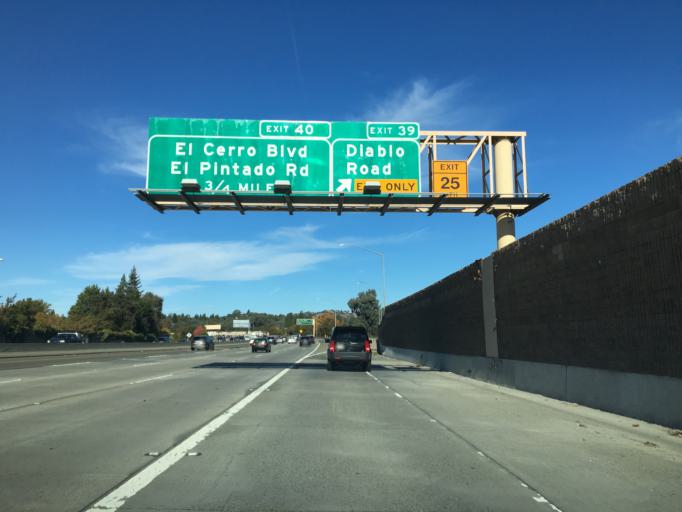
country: US
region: California
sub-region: Contra Costa County
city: Danville
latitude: 37.8191
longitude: -121.9930
